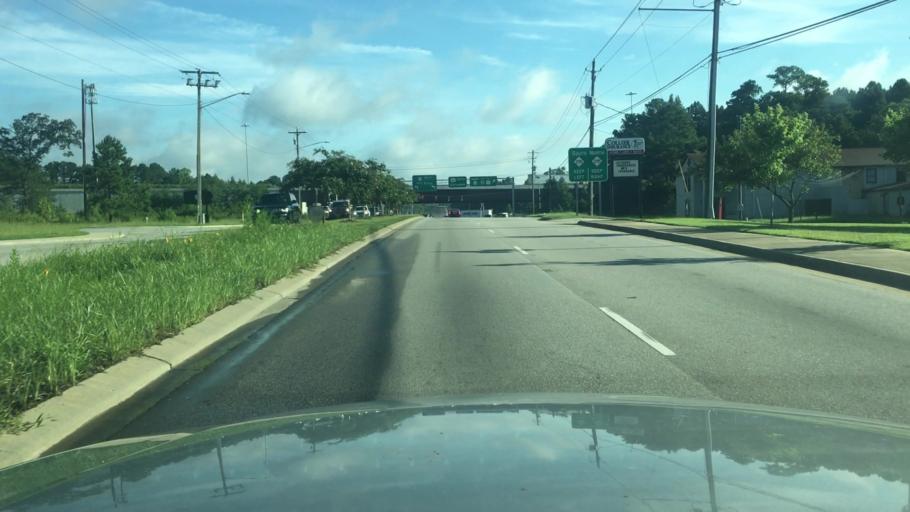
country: US
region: North Carolina
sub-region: Cumberland County
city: Eastover
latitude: 35.1522
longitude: -78.8703
